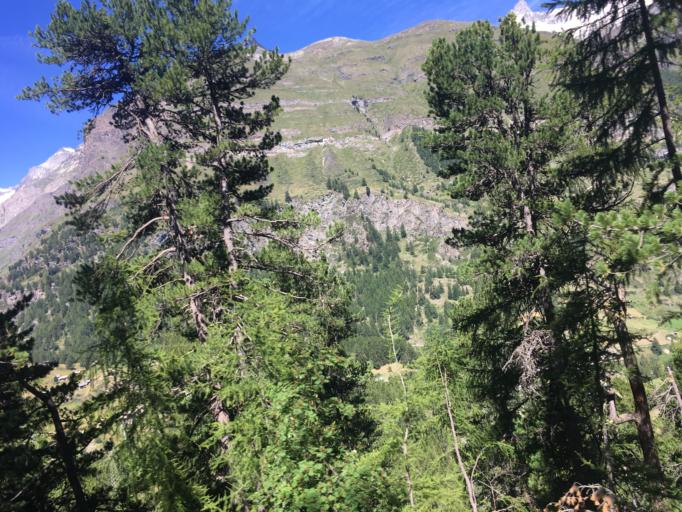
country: CH
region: Valais
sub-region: Visp District
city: Zermatt
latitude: 46.0054
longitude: 7.7447
